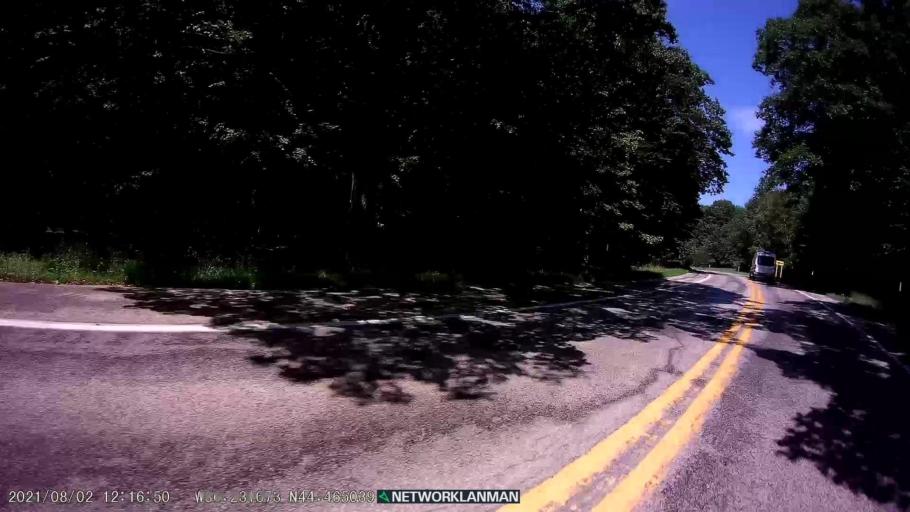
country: US
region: Michigan
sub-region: Benzie County
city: Frankfort
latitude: 44.4653
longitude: -86.2312
